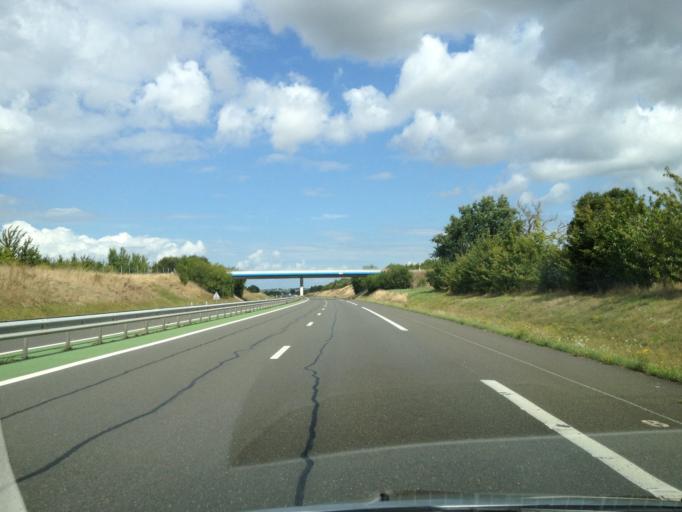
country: FR
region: Pays de la Loire
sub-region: Departement de Maine-et-Loire
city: Saint-Lambert-du-Lattay
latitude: 47.2704
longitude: -0.6141
